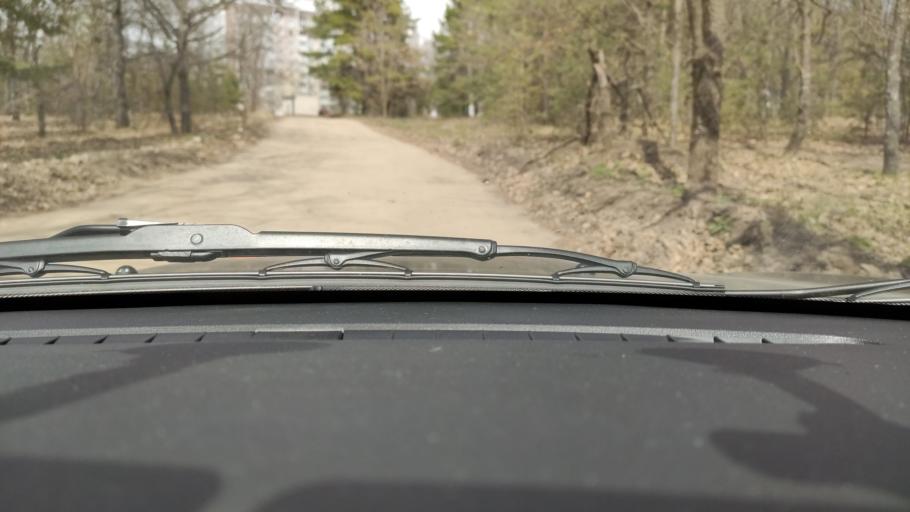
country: RU
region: Voronezj
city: Shilovo
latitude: 51.5564
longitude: 39.1162
